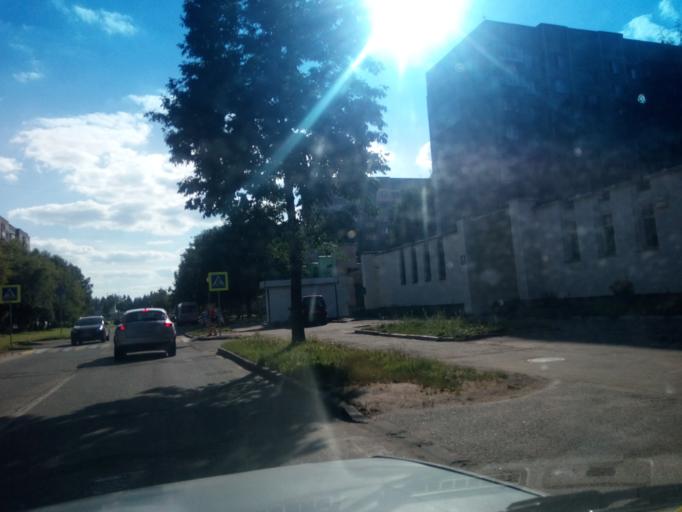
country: BY
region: Vitebsk
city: Navapolatsk
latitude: 55.5240
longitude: 28.6656
